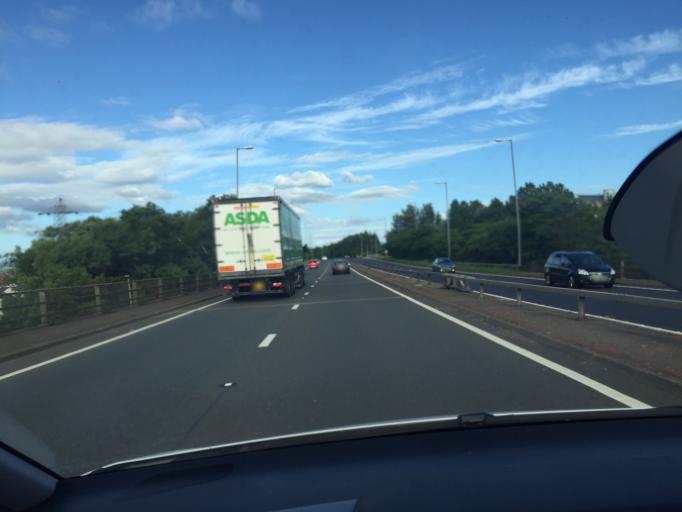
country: GB
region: Scotland
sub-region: South Lanarkshire
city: High Blantyre
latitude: 55.7826
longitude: -4.1049
